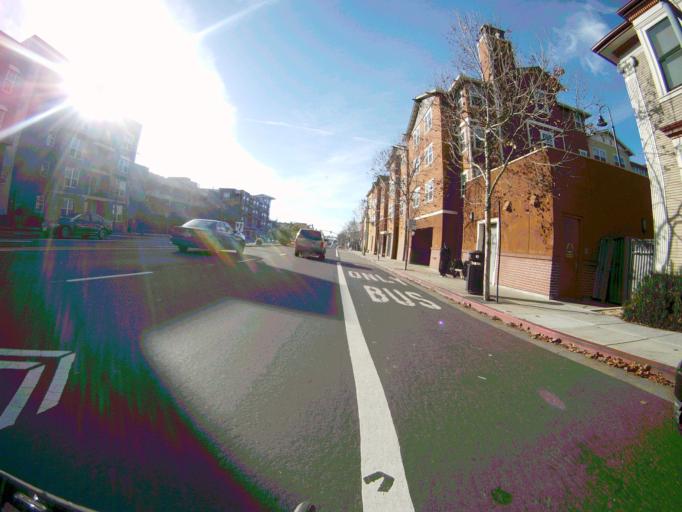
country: US
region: California
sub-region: Alameda County
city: Emeryville
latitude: 37.8313
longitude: -122.2782
